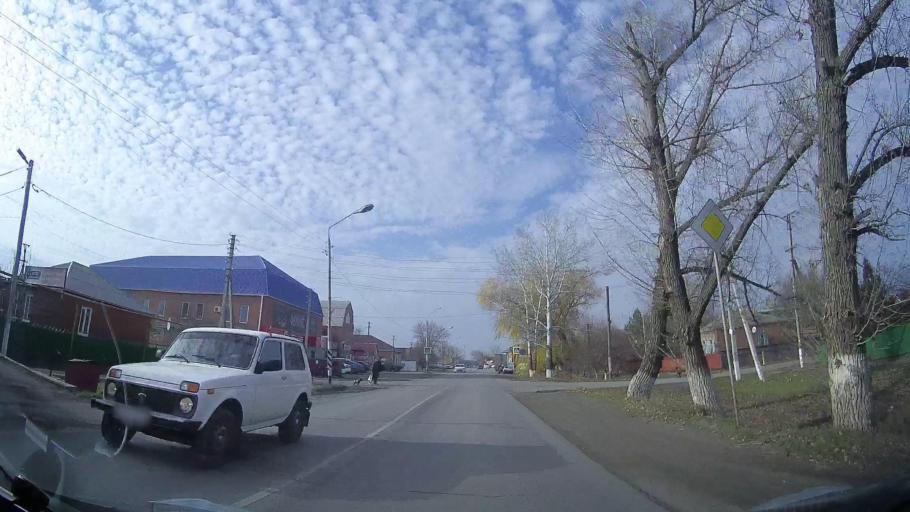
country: RU
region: Rostov
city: Veselyy
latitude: 47.0908
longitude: 40.7448
